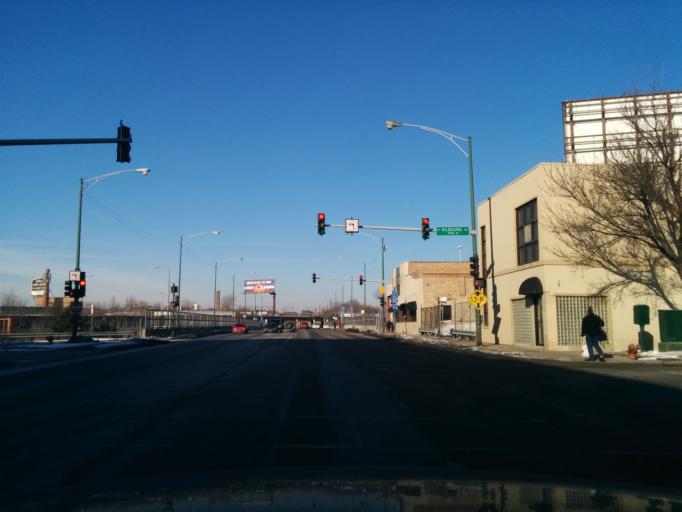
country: US
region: Illinois
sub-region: Cook County
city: Lincolnwood
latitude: 41.9608
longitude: -87.7409
